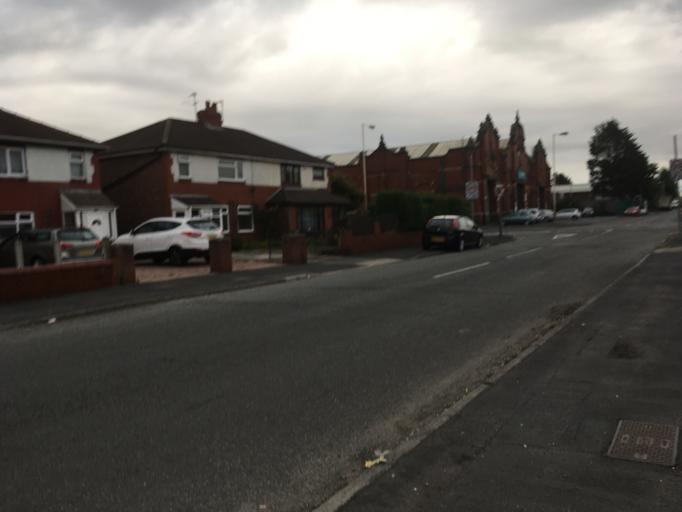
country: GB
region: England
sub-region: Sefton
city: Southport
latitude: 53.6445
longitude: -2.9680
